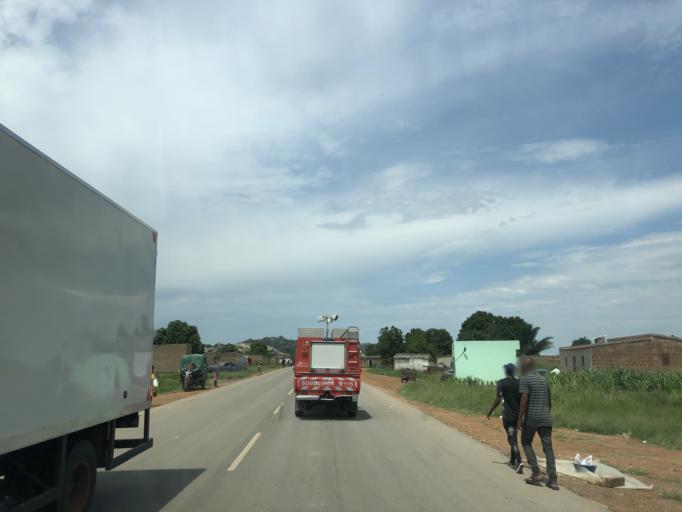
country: AO
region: Cuanza Sul
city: Quibala
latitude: -10.7359
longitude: 14.9929
